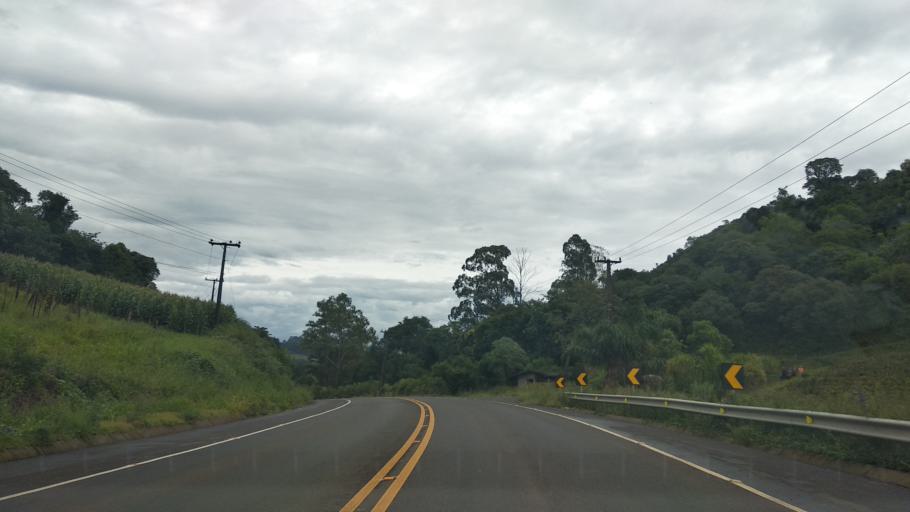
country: BR
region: Santa Catarina
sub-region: Videira
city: Videira
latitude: -27.0468
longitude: -51.1630
